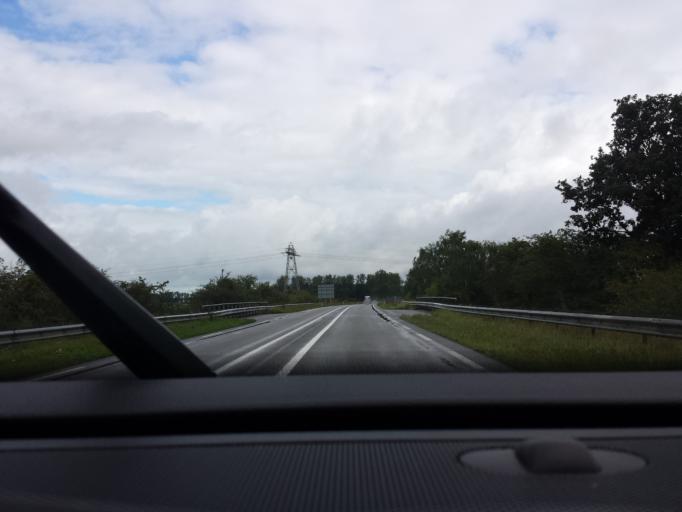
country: NL
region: Gelderland
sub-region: Gemeente Lochem
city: Laren
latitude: 52.2541
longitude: 6.3988
